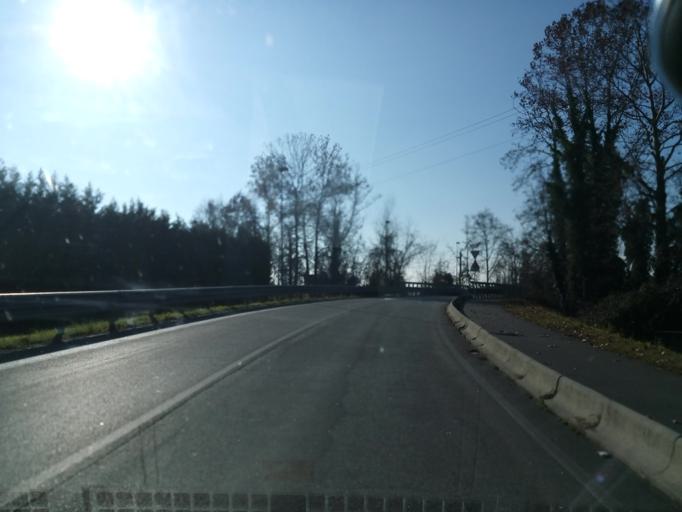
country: IT
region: Veneto
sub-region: Provincia di Treviso
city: Lancenigo-Villorba
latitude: 45.7328
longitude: 12.2577
